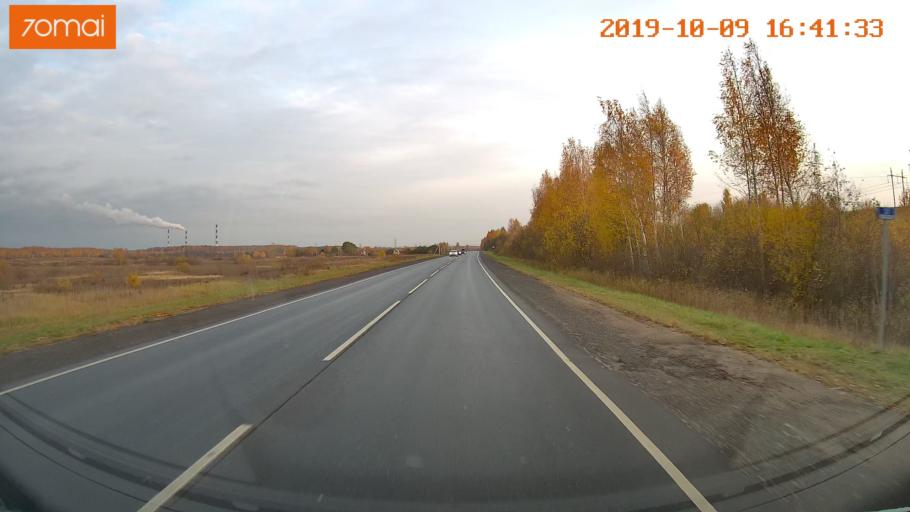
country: RU
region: Kostroma
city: Volgorechensk
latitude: 57.4720
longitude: 41.0831
